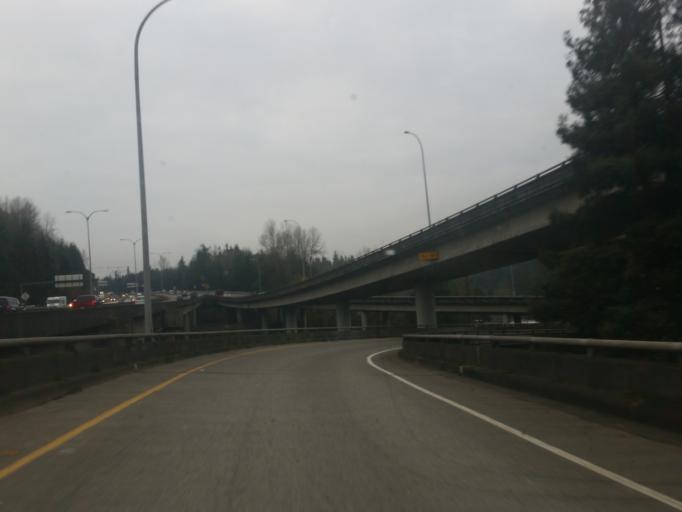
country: US
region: Washington
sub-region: King County
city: Bothell
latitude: 47.7577
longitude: -122.1848
